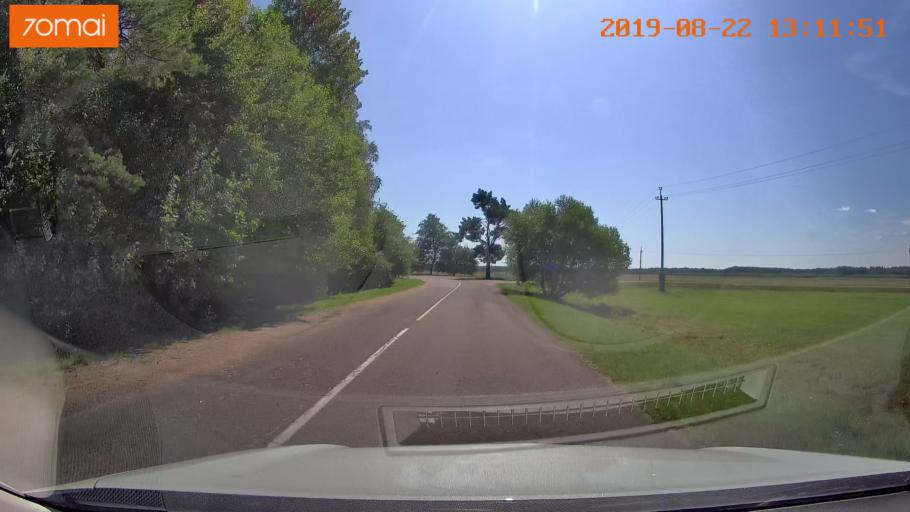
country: BY
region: Minsk
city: Prawdzinski
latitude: 53.2743
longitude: 27.8548
